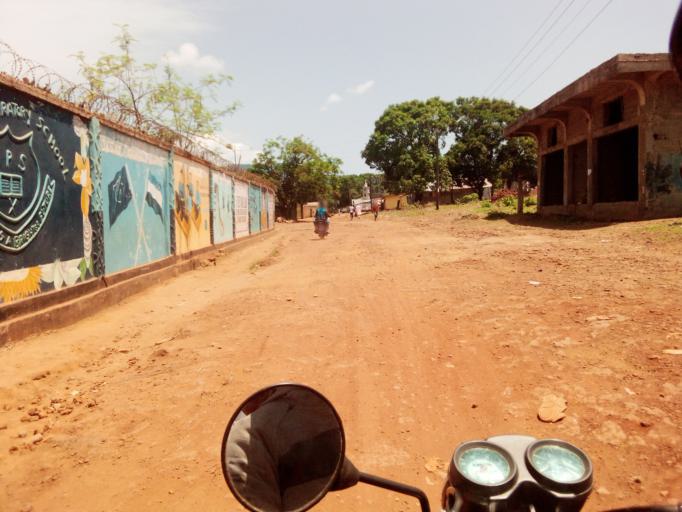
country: SL
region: Western Area
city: Waterloo
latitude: 8.3316
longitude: -13.0764
